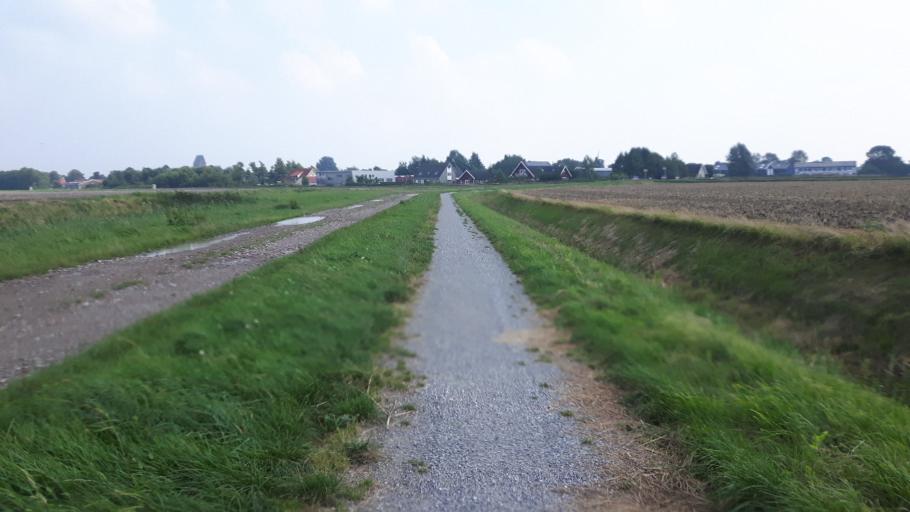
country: NL
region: Groningen
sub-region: Gemeente Appingedam
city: Appingedam
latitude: 53.3370
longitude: 6.7355
